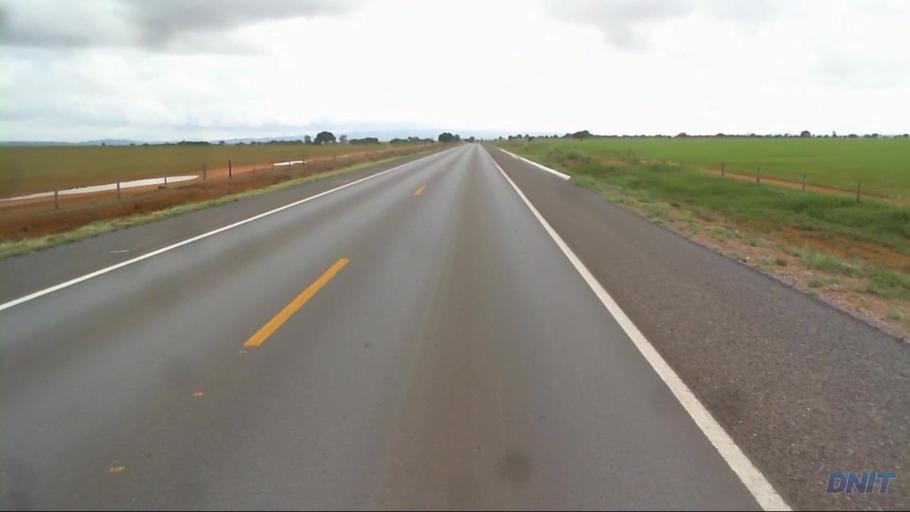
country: BR
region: Goias
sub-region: Padre Bernardo
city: Padre Bernardo
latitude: -15.2193
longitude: -48.6330
